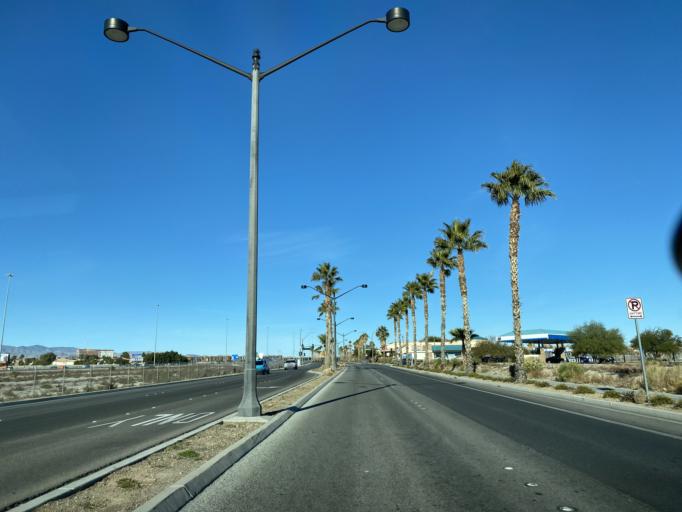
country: US
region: Nevada
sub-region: Clark County
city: Las Vegas
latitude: 36.2820
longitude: -115.2687
